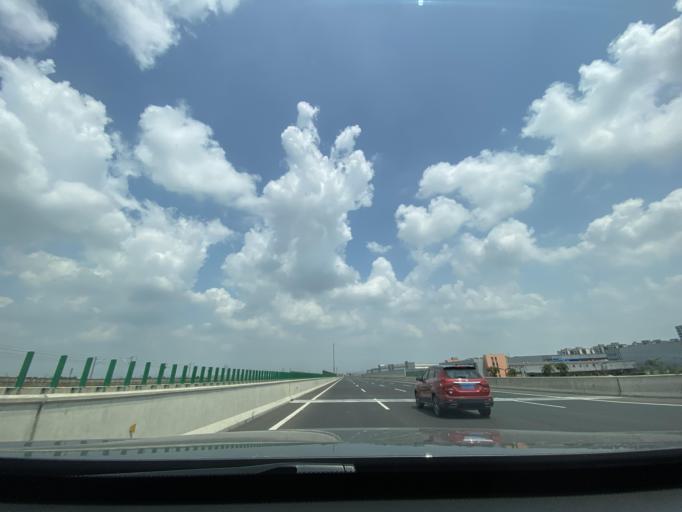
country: CN
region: Sichuan
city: Longquan
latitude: 30.5235
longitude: 104.1719
